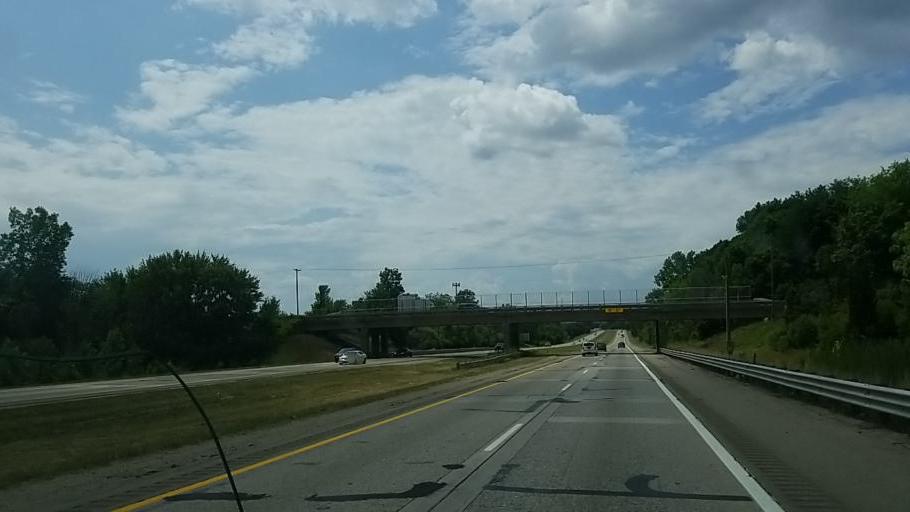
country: US
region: Michigan
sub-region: Kent County
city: East Grand Rapids
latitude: 42.9769
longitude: -85.6092
